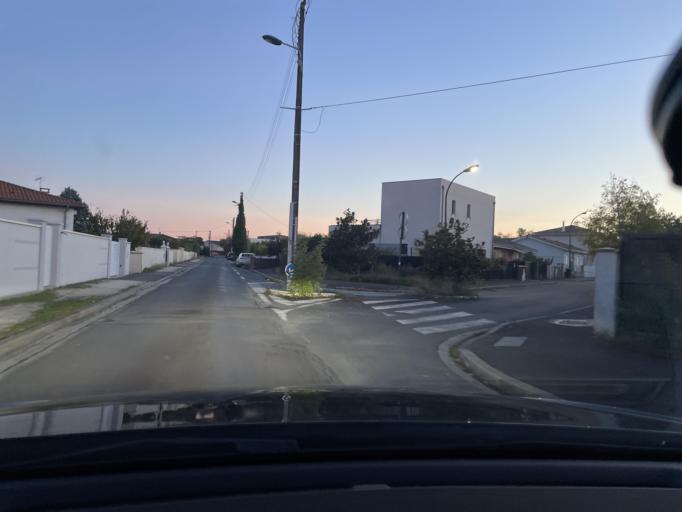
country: FR
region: Aquitaine
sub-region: Departement de la Gironde
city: Bruges
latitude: 44.8828
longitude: -0.5961
